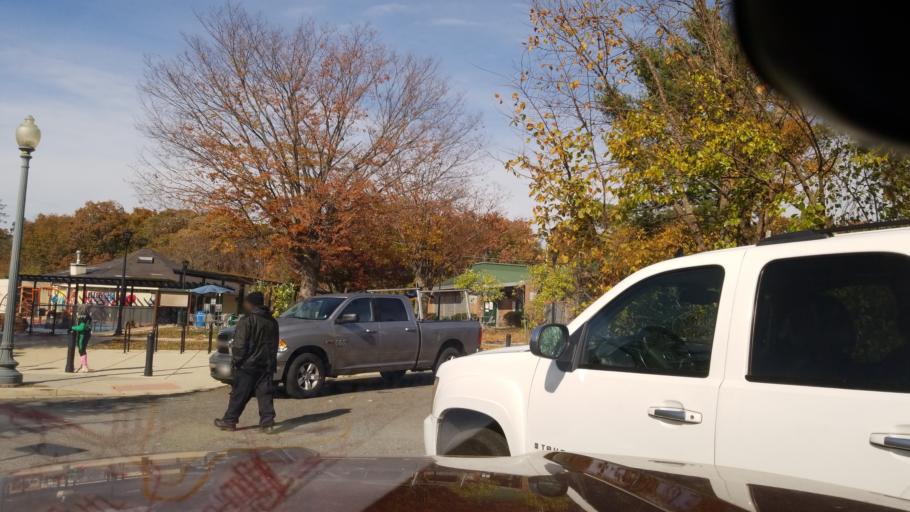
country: US
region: Maryland
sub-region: Prince George's County
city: Hillcrest Heights
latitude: 38.8521
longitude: -76.9772
